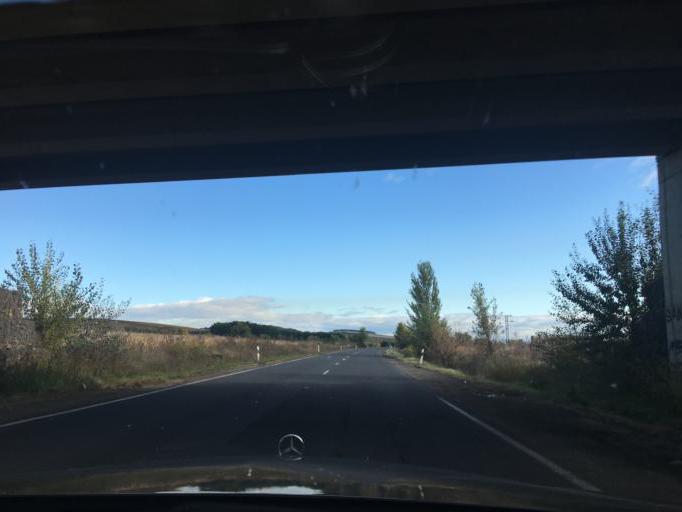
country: HU
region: Borsod-Abauj-Zemplen
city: Gonc
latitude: 48.5029
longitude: 21.2220
